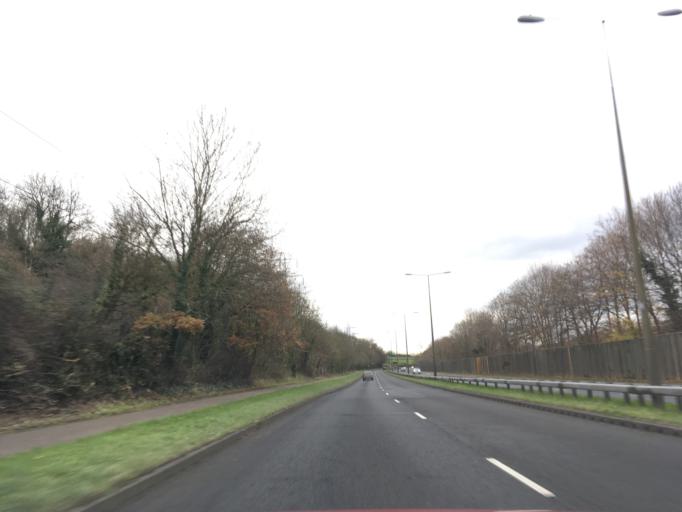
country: GB
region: Wales
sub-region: Newport
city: Llanwern
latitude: 51.5901
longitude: -2.9251
